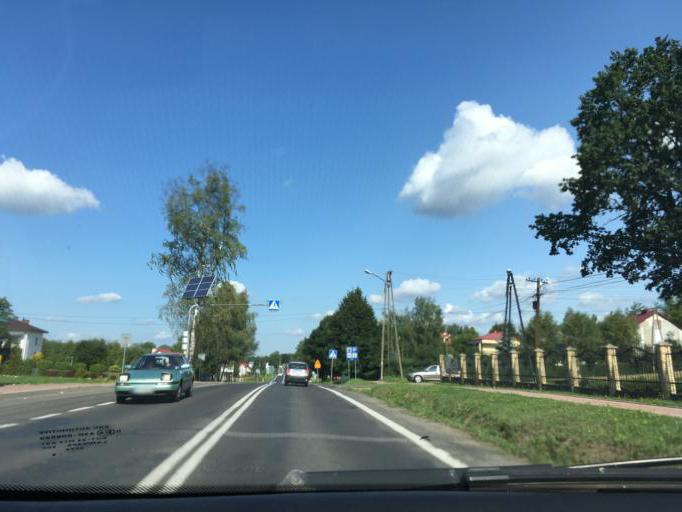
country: PL
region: Subcarpathian Voivodeship
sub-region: Powiat sanocki
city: Sanok
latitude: 49.5322
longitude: 22.2295
